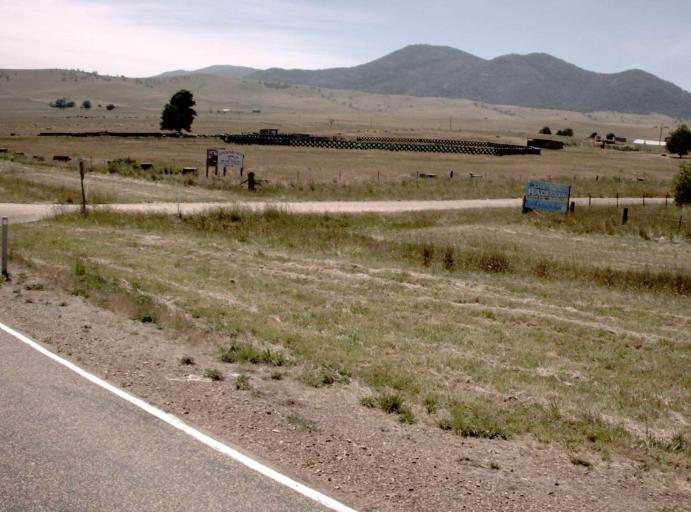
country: AU
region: Victoria
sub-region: Alpine
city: Mount Beauty
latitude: -37.0033
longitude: 147.6669
